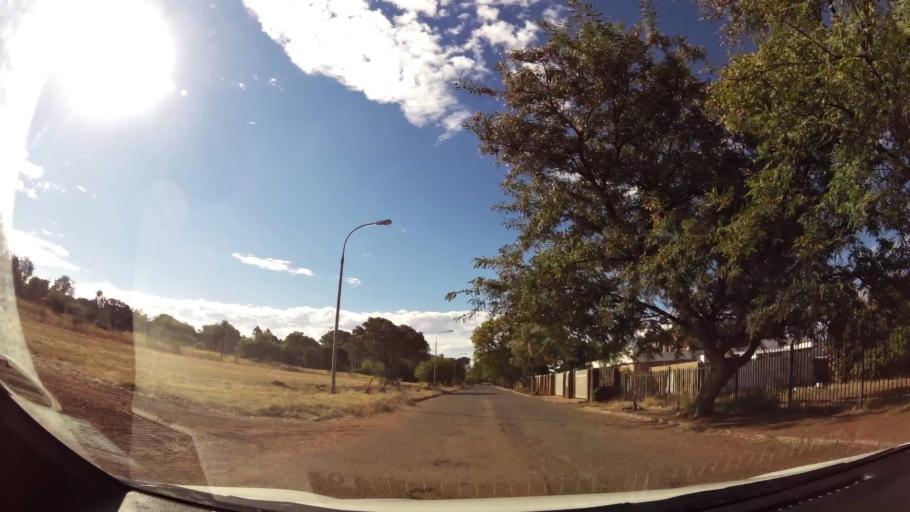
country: ZA
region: Limpopo
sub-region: Waterberg District Municipality
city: Warmbaths
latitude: -24.8787
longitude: 28.2756
